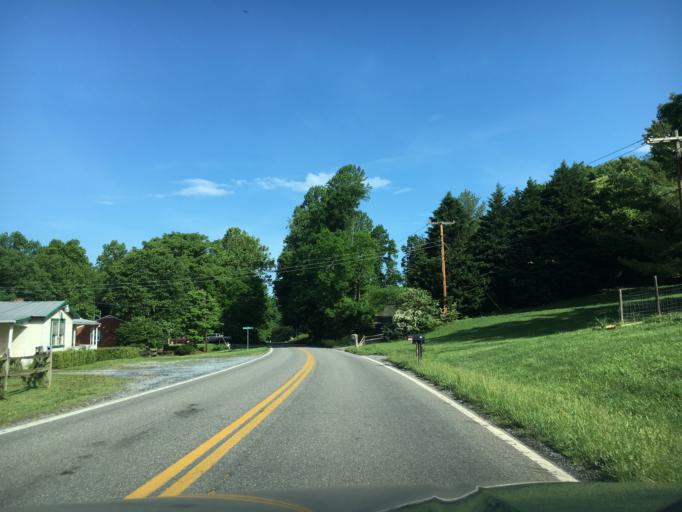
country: US
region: Virginia
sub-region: Campbell County
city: Rustburg
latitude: 37.3032
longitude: -79.1634
